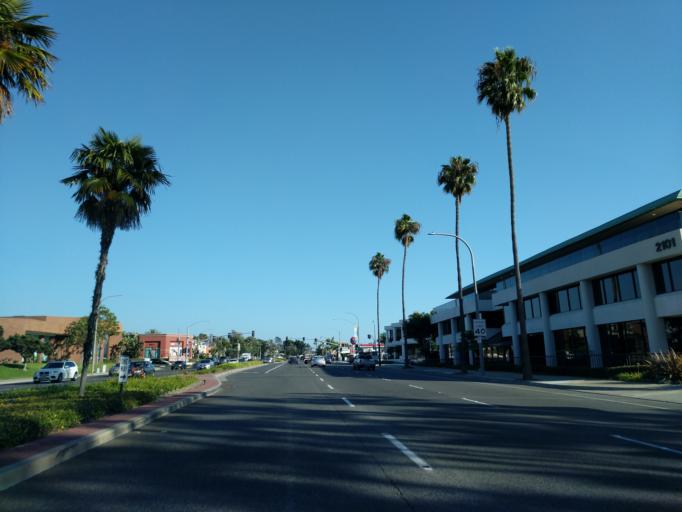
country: US
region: California
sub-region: Orange County
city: San Joaquin Hills
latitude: 33.6065
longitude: -117.8772
